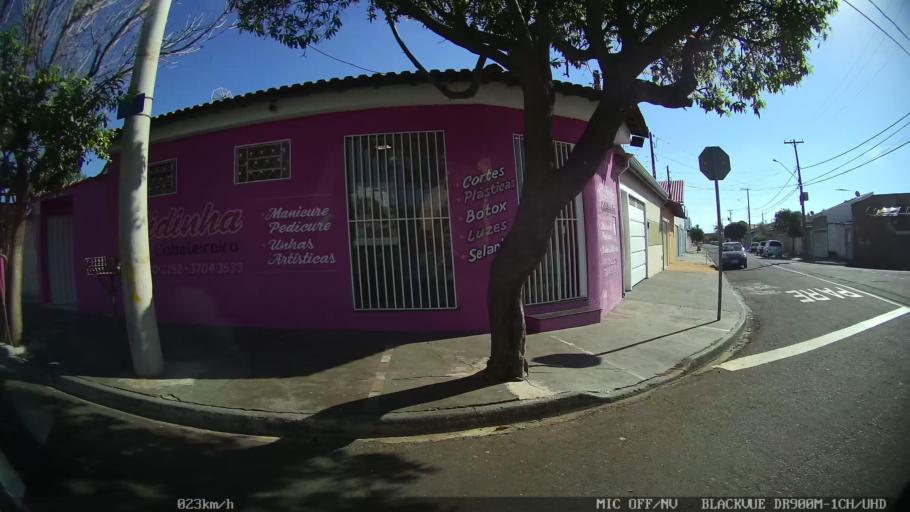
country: BR
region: Sao Paulo
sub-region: Franca
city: Franca
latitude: -20.4883
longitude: -47.4154
